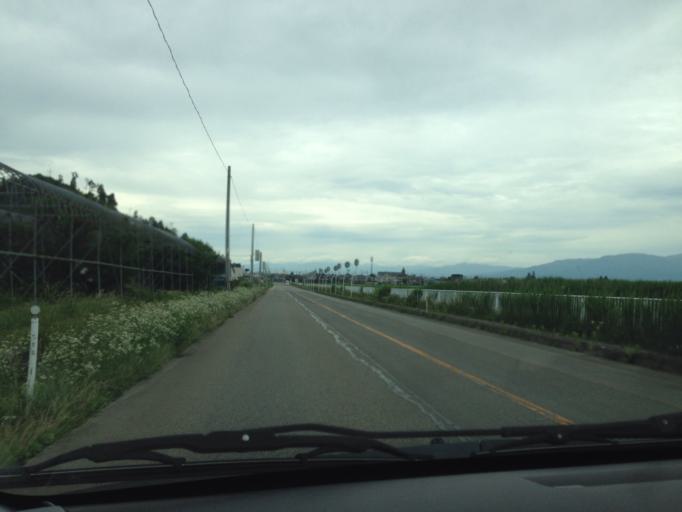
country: JP
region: Fukushima
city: Kitakata
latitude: 37.4422
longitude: 139.8813
